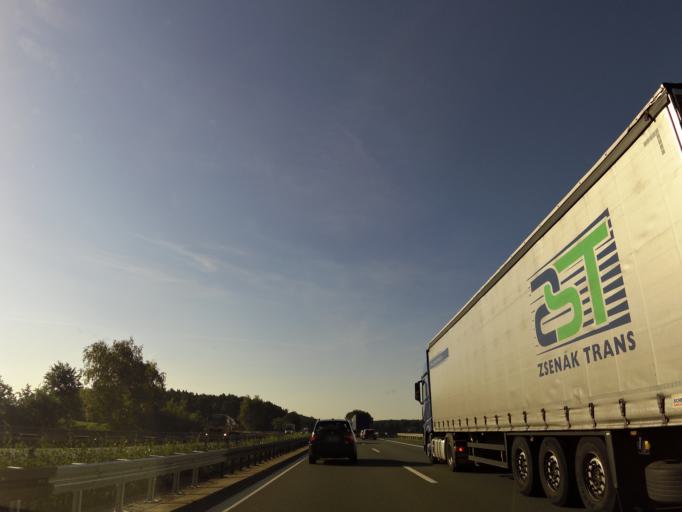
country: DE
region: Bavaria
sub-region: Regierungsbezirk Mittelfranken
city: Hessdorf
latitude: 49.6487
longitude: 10.9037
